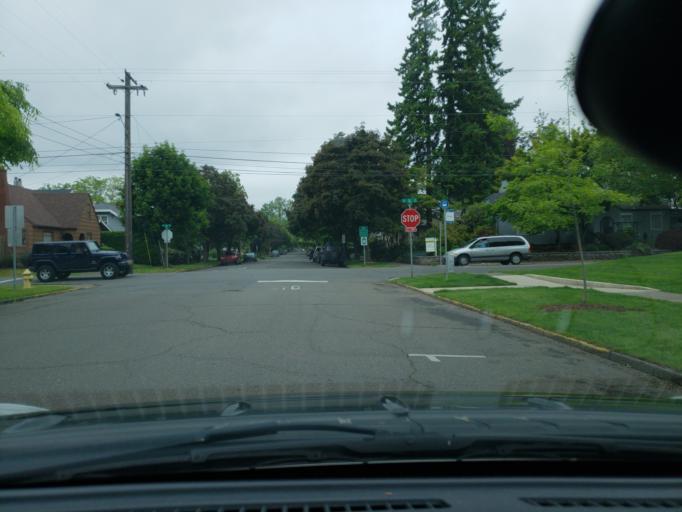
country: US
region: Oregon
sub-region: Marion County
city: Salem
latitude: 44.9469
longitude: -123.0280
